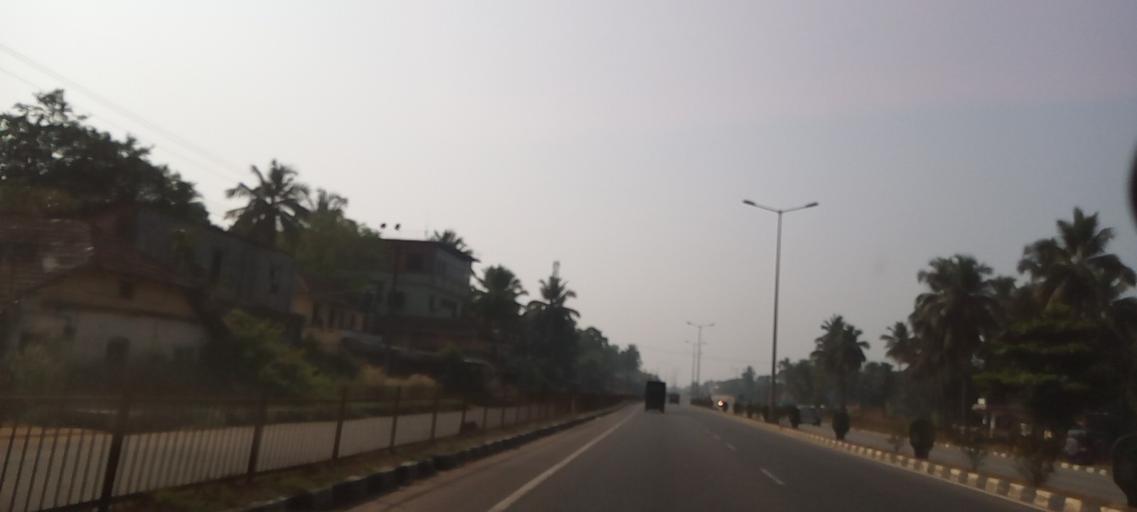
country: IN
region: Karnataka
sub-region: Udupi
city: Coondapoor
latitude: 13.5327
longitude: 74.7044
